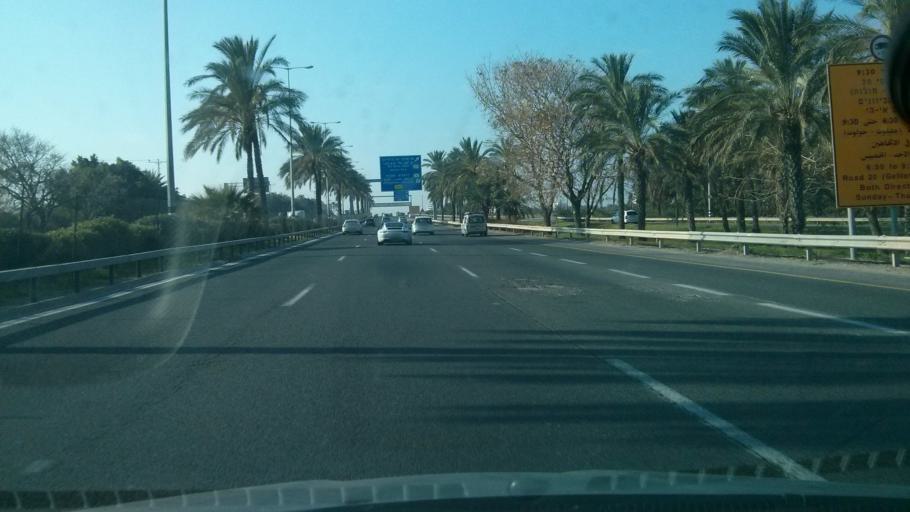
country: IL
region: Tel Aviv
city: Herzliya Pituah
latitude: 32.1552
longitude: 34.8078
